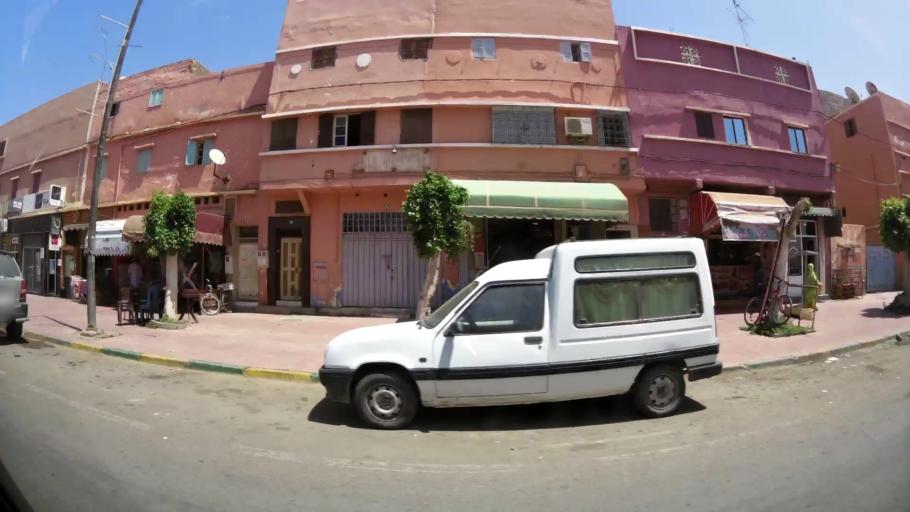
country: MA
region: Souss-Massa-Draa
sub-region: Inezgane-Ait Mellou
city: Inezgane
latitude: 30.3421
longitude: -9.4977
